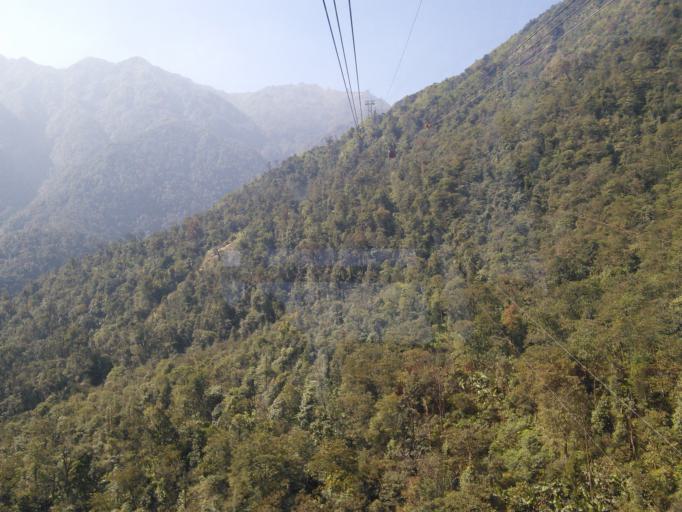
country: VN
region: Lao Cai
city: Sa Pa
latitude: 22.3237
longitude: 103.8021
